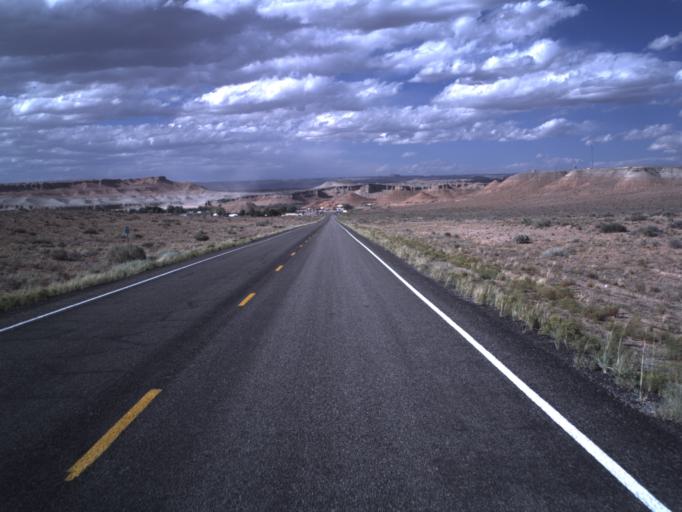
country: US
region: Utah
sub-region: Emery County
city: Ferron
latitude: 38.3600
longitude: -110.6988
